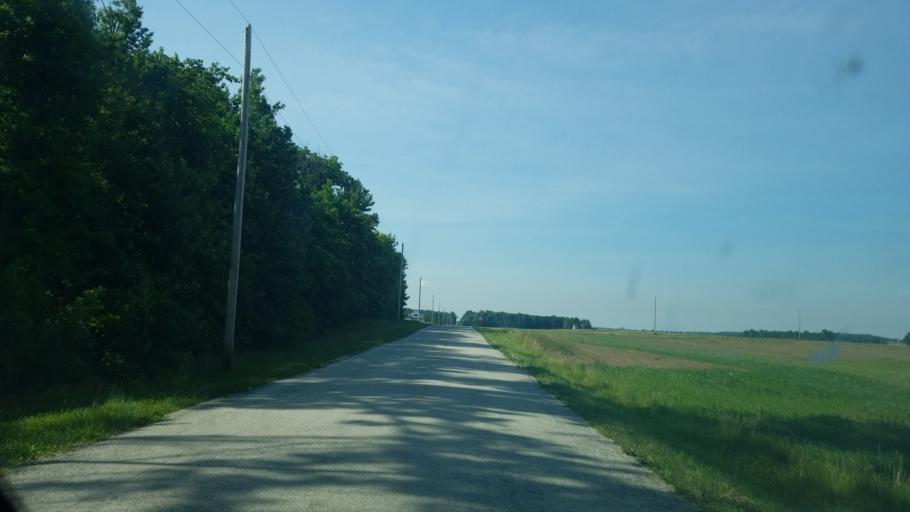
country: US
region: Ohio
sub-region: Wyandot County
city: Carey
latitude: 41.0274
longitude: -83.3629
